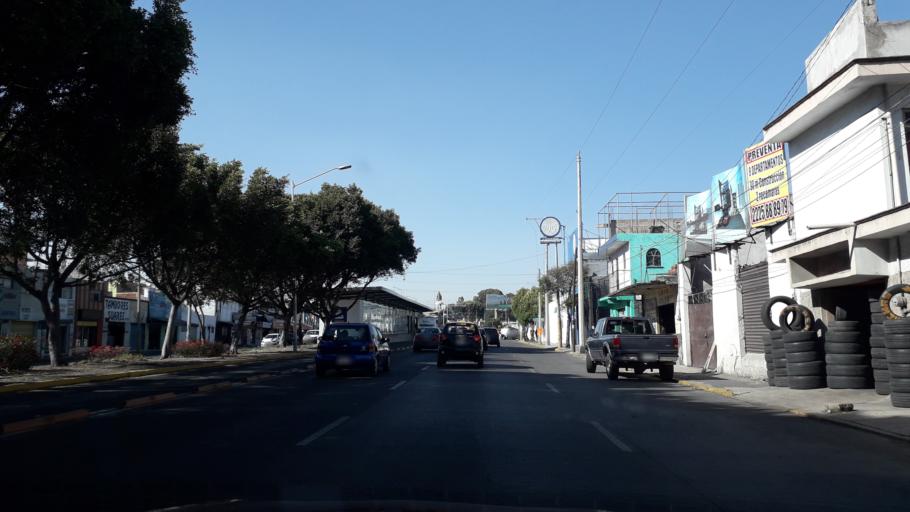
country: MX
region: Puebla
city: Puebla
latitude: 19.0630
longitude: -98.1917
